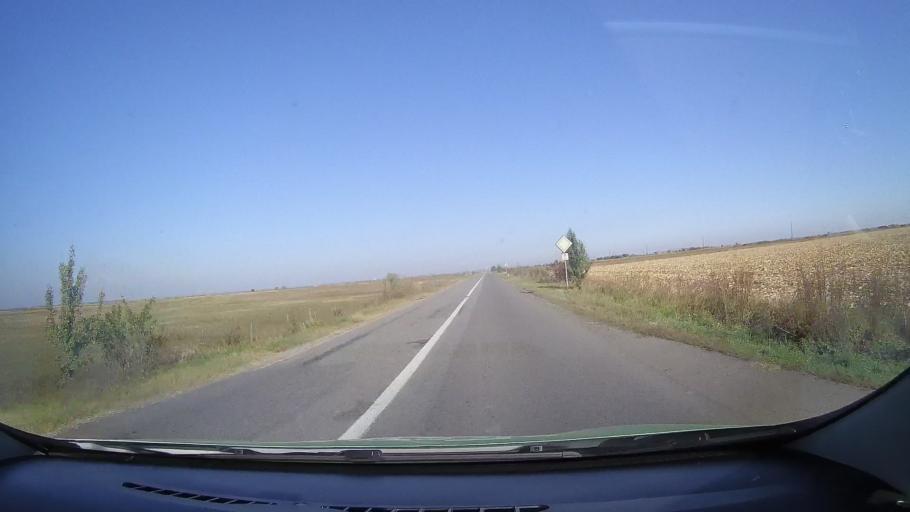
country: RO
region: Satu Mare
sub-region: Comuna Cauas
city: Cauas
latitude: 47.5362
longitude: 22.5648
